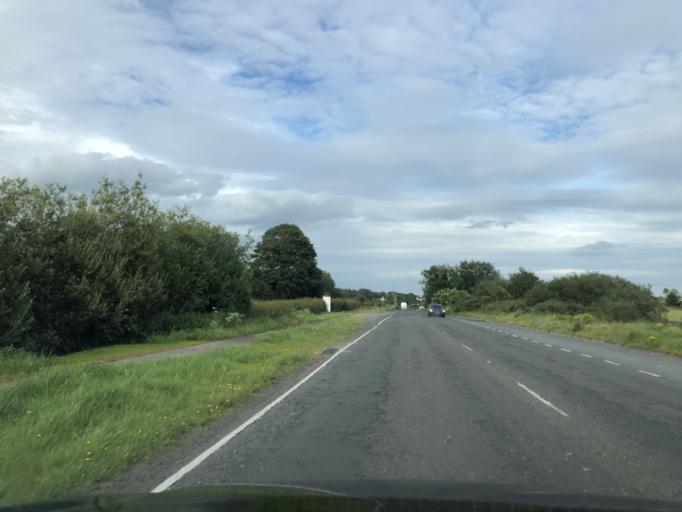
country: GB
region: Northern Ireland
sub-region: Down District
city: Castlewellan
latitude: 54.2485
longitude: -5.9703
